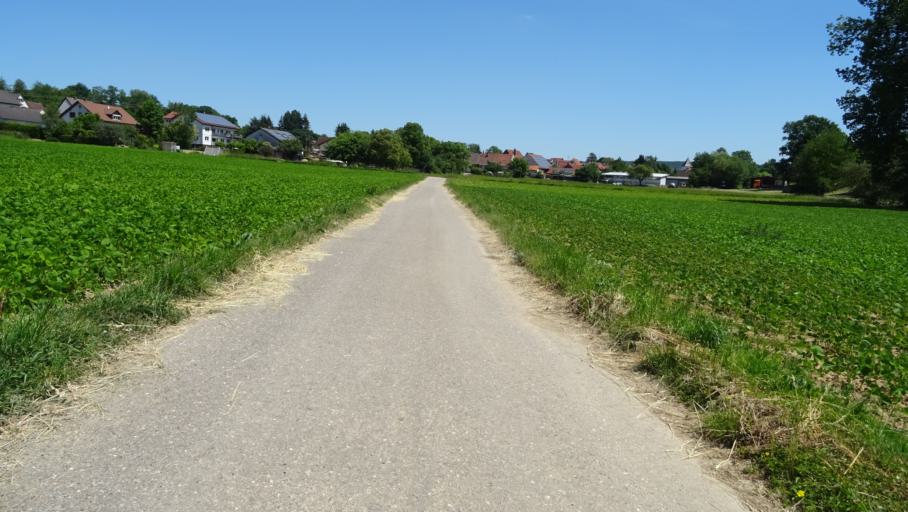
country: DE
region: Baden-Wuerttemberg
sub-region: Karlsruhe Region
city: Aglasterhausen
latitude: 49.3423
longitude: 9.0179
